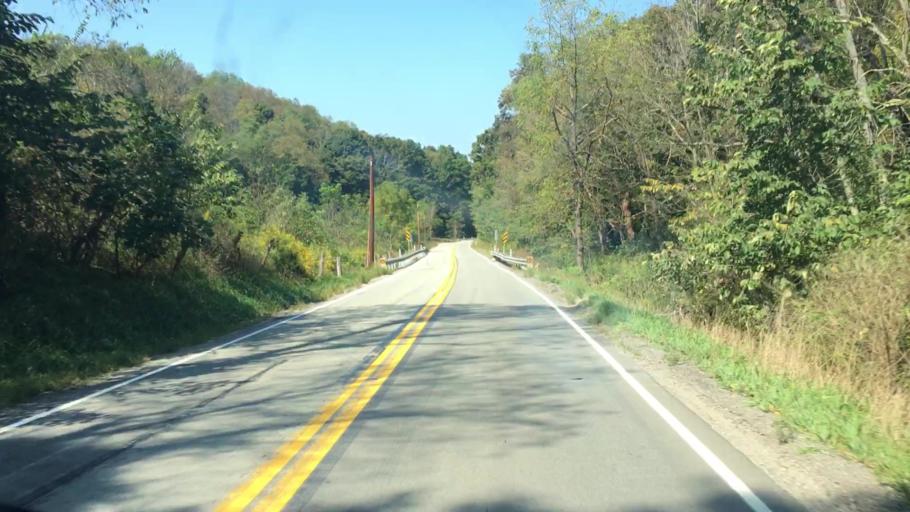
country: US
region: Pennsylvania
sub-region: Greene County
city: Waynesburg
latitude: 39.9927
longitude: -80.3503
